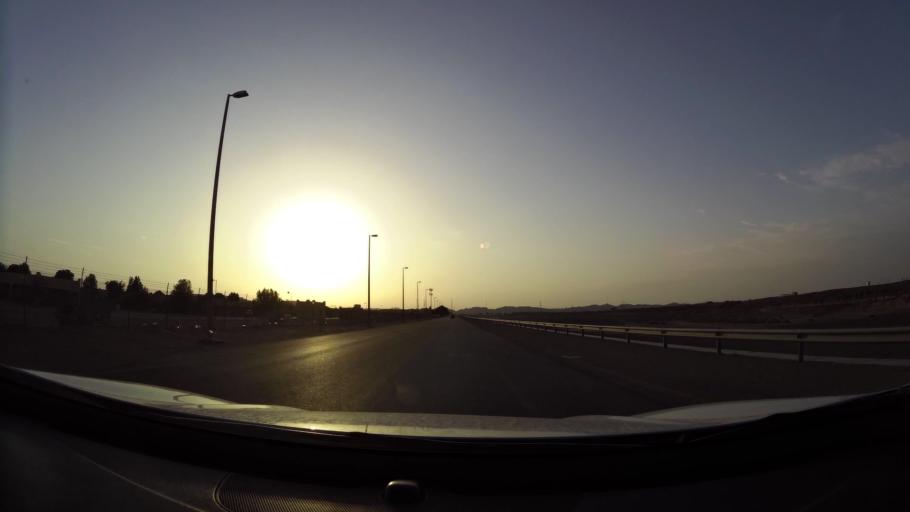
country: AE
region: Abu Dhabi
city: Al Ain
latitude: 24.1643
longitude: 55.8155
